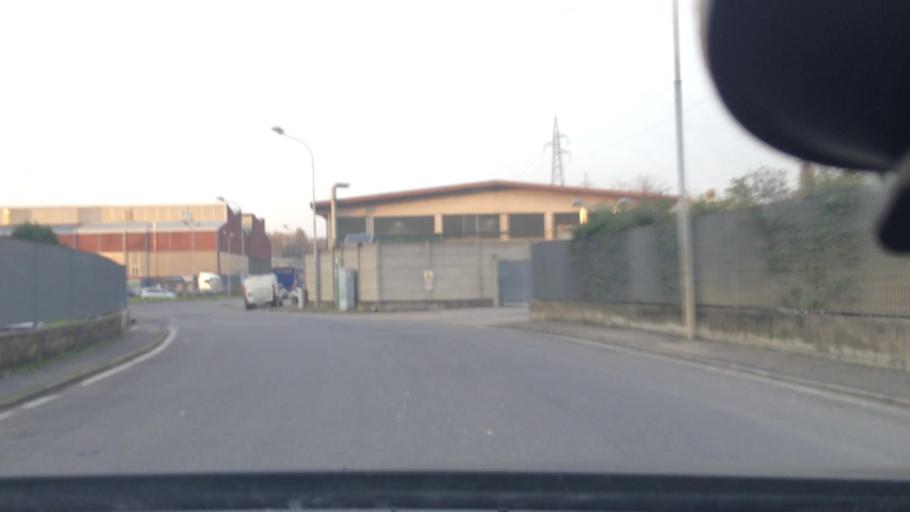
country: IT
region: Lombardy
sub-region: Provincia di Monza e Brianza
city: Villaggio del Sole
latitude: 45.6282
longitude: 9.1039
